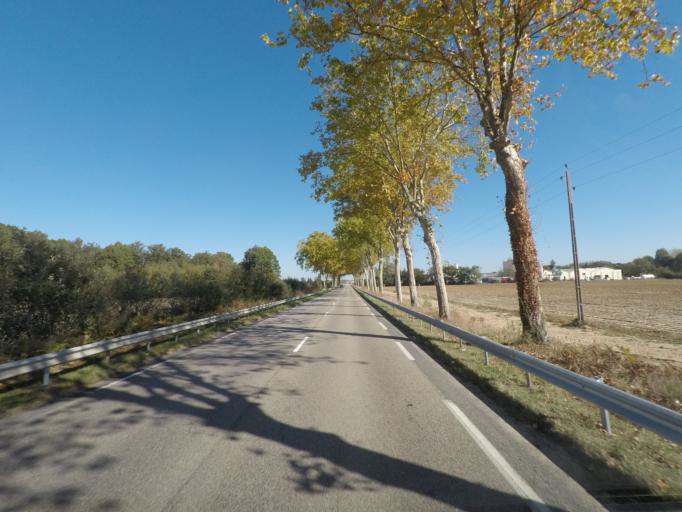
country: FR
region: Rhone-Alpes
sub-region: Departement de l'Ain
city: Servas
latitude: 46.1236
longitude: 5.1580
